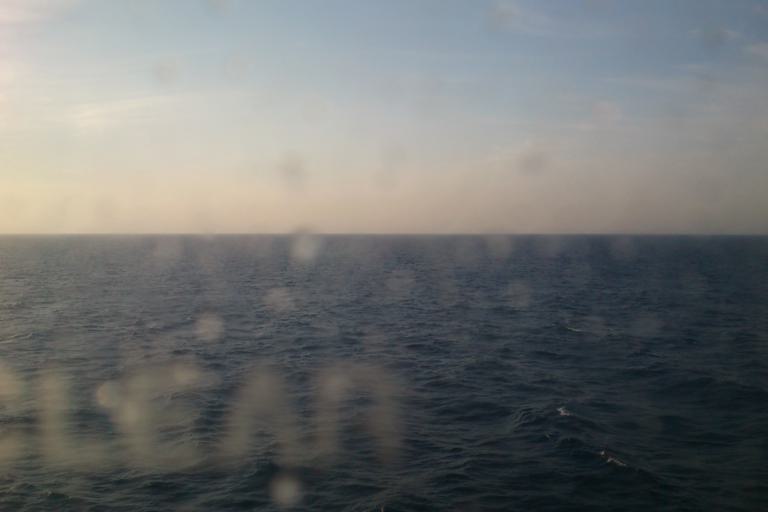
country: JP
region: Ishikawa
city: Nanao
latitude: 37.7241
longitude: 136.3912
